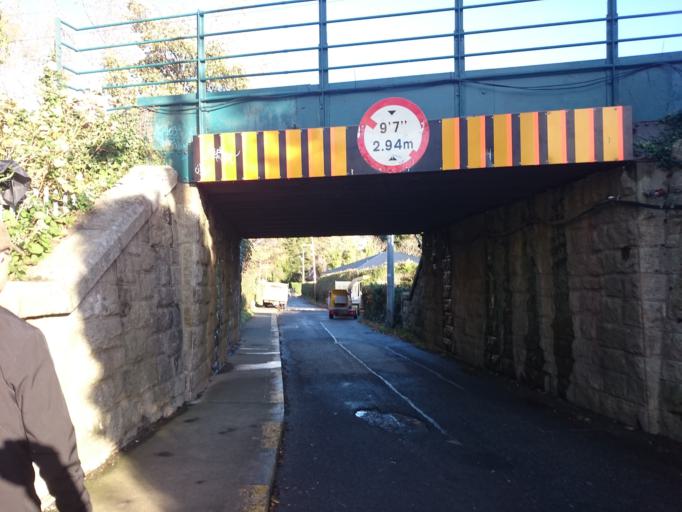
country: IE
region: Leinster
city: Shankill
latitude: 53.2320
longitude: -6.1153
